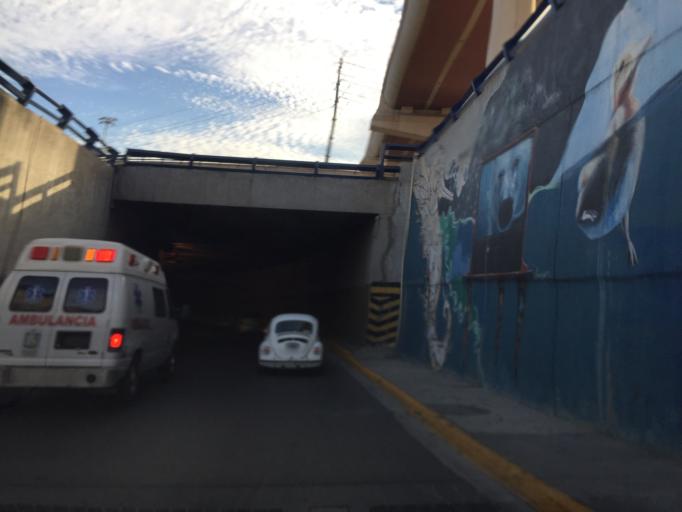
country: MX
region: Nuevo Leon
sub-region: San Nicolas de los Garza
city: San Nicolas de los Garza
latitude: 25.7323
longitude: -100.3053
